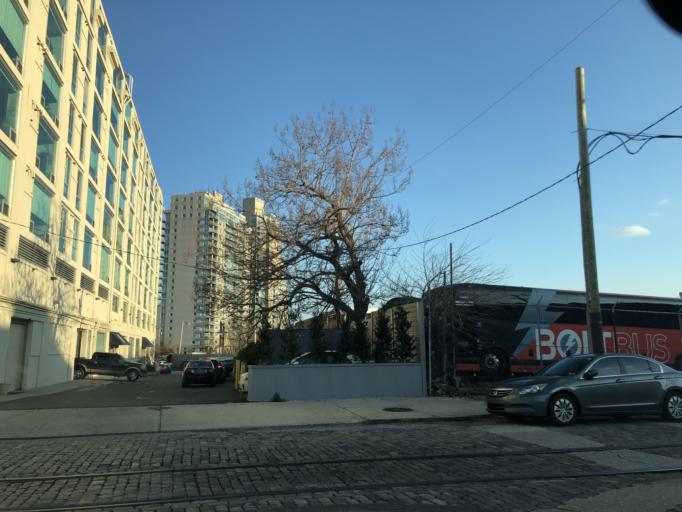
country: US
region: Pennsylvania
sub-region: Philadelphia County
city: Philadelphia
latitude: 39.9623
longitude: -75.1384
